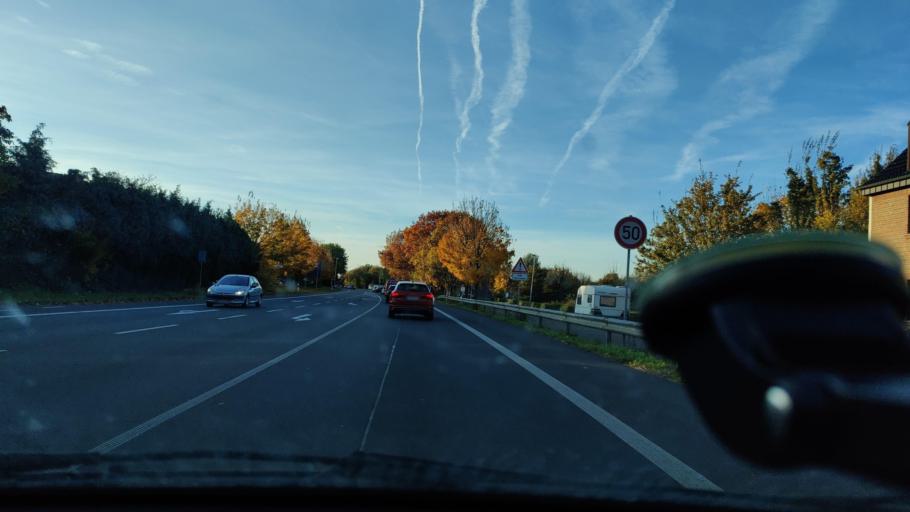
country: DE
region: North Rhine-Westphalia
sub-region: Regierungsbezirk Dusseldorf
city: Korschenbroich
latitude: 51.2266
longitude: 6.4763
